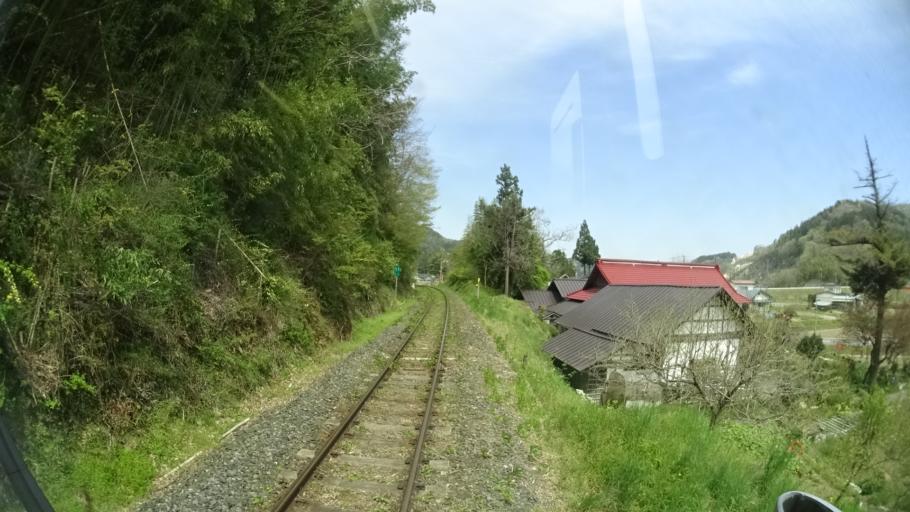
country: JP
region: Iwate
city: Ichinoseki
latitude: 38.9596
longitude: 141.2442
